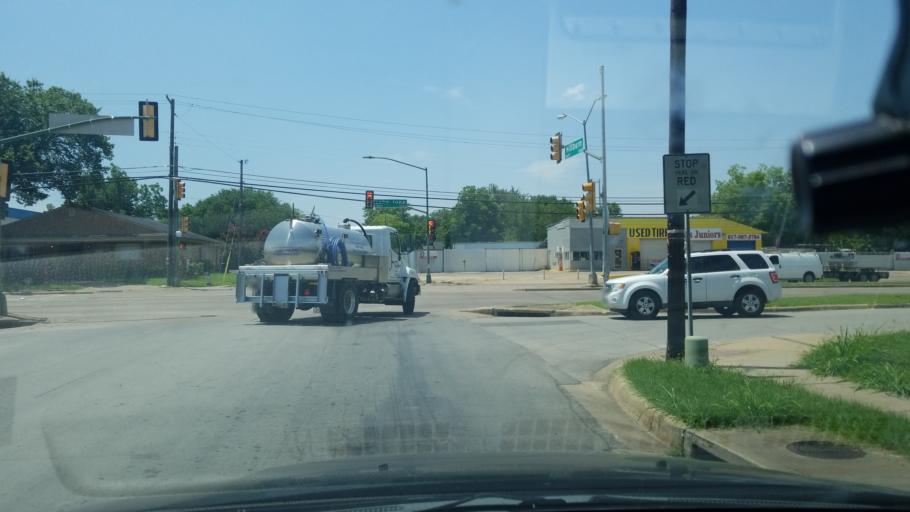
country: US
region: Texas
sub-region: Dallas County
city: Balch Springs
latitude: 32.7346
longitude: -96.6884
